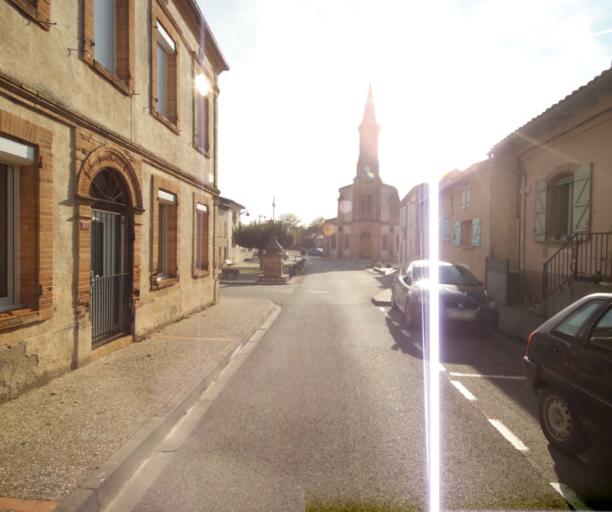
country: FR
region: Midi-Pyrenees
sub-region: Departement de la Haute-Garonne
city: Villemur-sur-Tarn
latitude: 43.9015
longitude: 1.4961
